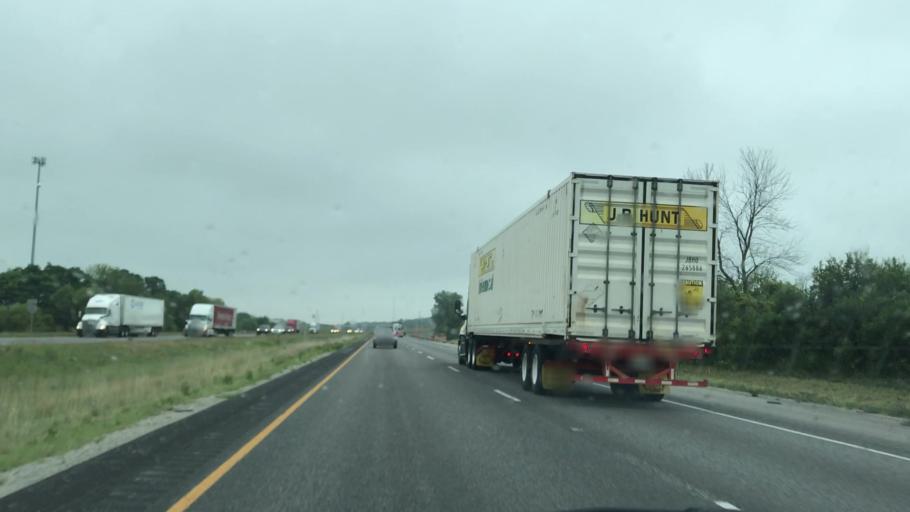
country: US
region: Indiana
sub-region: Boone County
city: Lebanon
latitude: 40.1194
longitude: -86.5155
